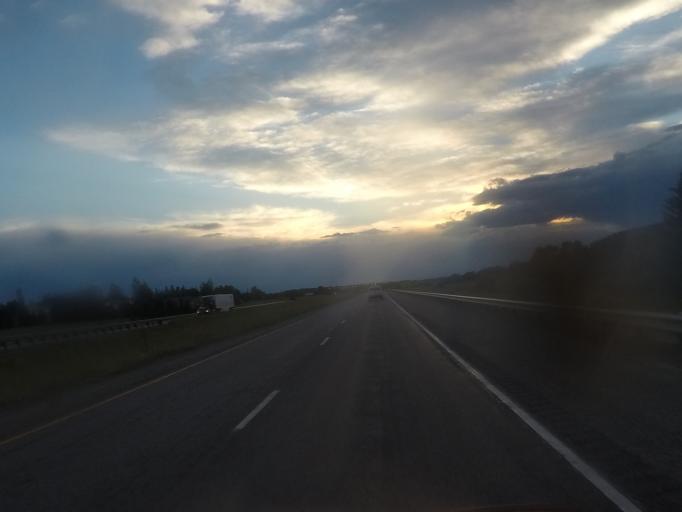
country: US
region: Montana
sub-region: Gallatin County
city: Bozeman
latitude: 45.6665
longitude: -110.9807
